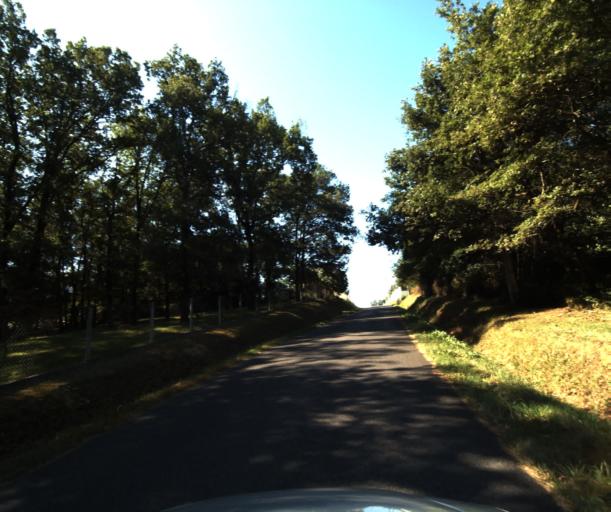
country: FR
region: Midi-Pyrenees
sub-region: Departement de la Haute-Garonne
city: Eaunes
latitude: 43.4401
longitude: 1.3682
